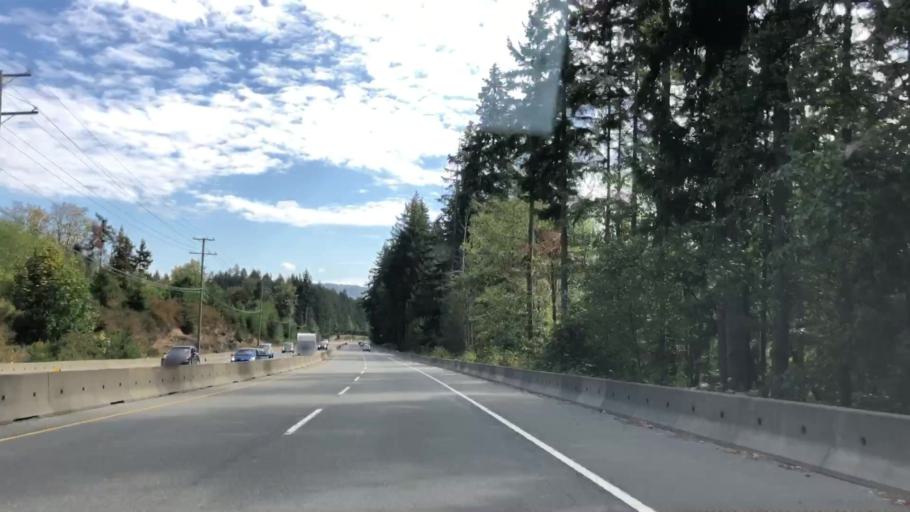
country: CA
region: British Columbia
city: North Cowichan
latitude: 48.8924
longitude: -123.7107
